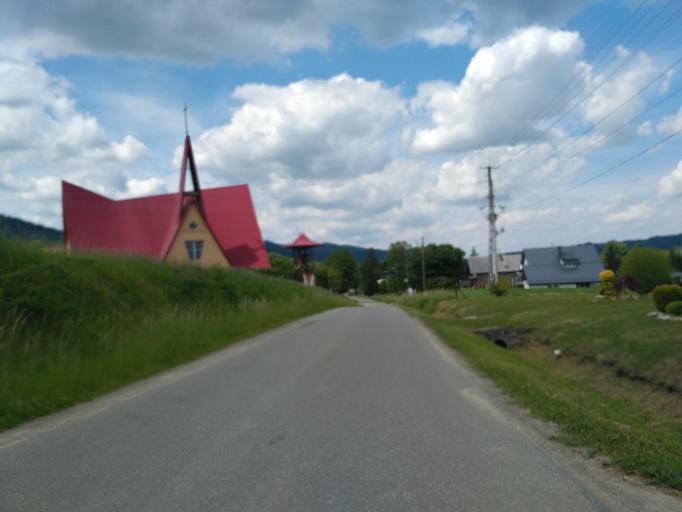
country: PL
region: Subcarpathian Voivodeship
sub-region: Powiat krosnienski
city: Dukla
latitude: 49.5543
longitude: 21.6278
